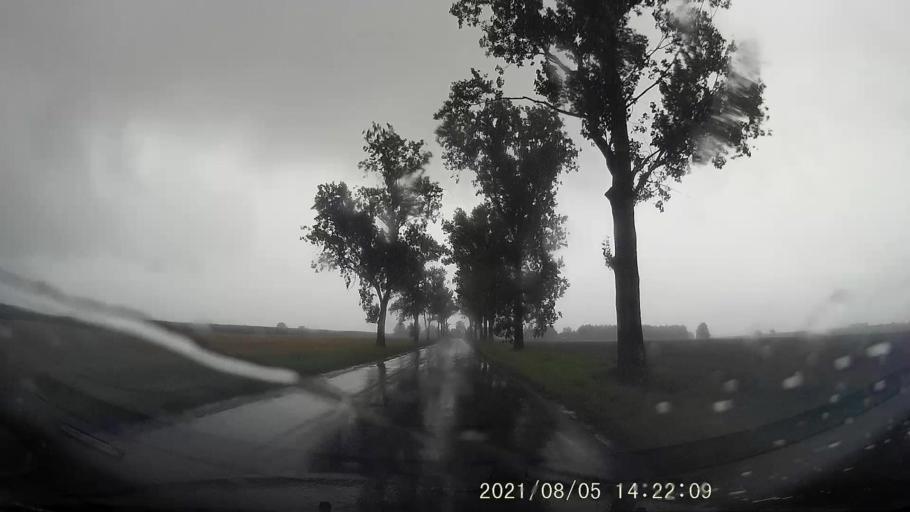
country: PL
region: Opole Voivodeship
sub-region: Powiat nyski
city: Korfantow
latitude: 50.4750
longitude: 17.6609
